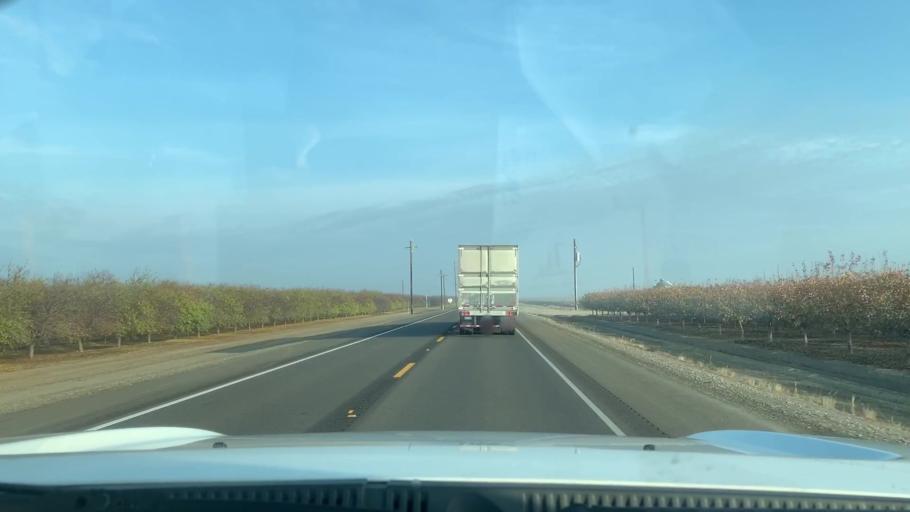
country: US
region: California
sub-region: Kings County
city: Kettleman City
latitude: 36.0195
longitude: -119.9592
